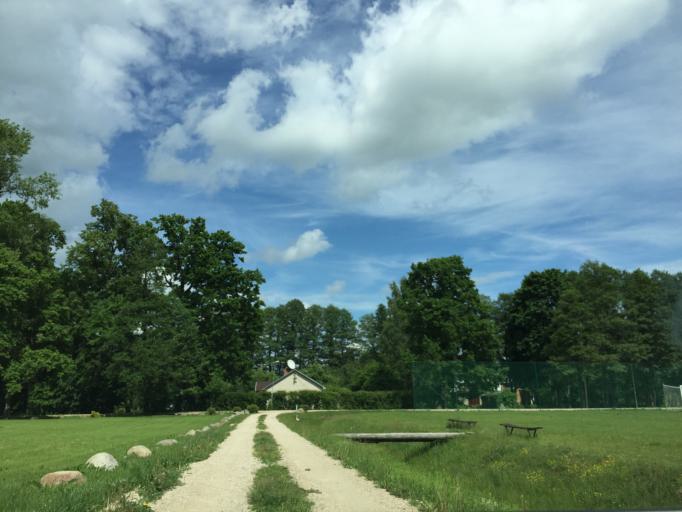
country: LV
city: Tireli
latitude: 56.6886
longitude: 23.4899
